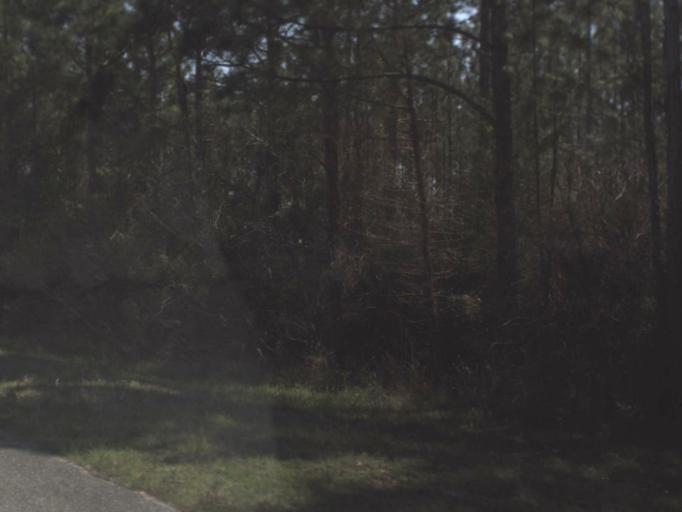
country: US
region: Florida
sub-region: Gulf County
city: Port Saint Joe
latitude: 29.7506
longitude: -85.2451
